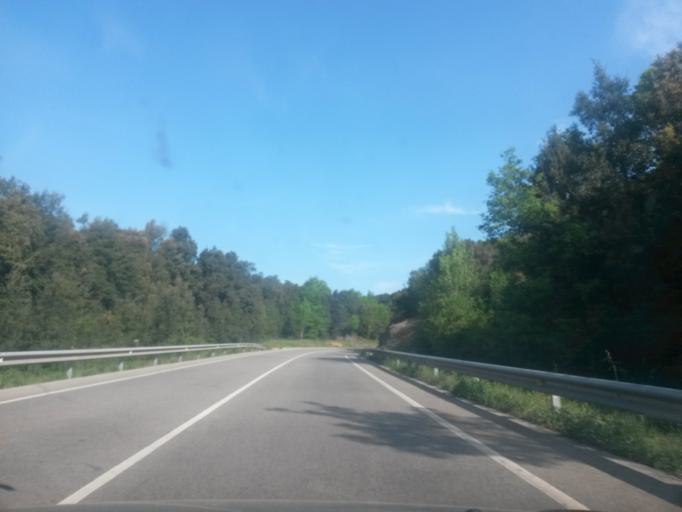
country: ES
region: Catalonia
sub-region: Provincia de Girona
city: Sant Feliu de Pallerols
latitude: 42.0687
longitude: 2.5245
